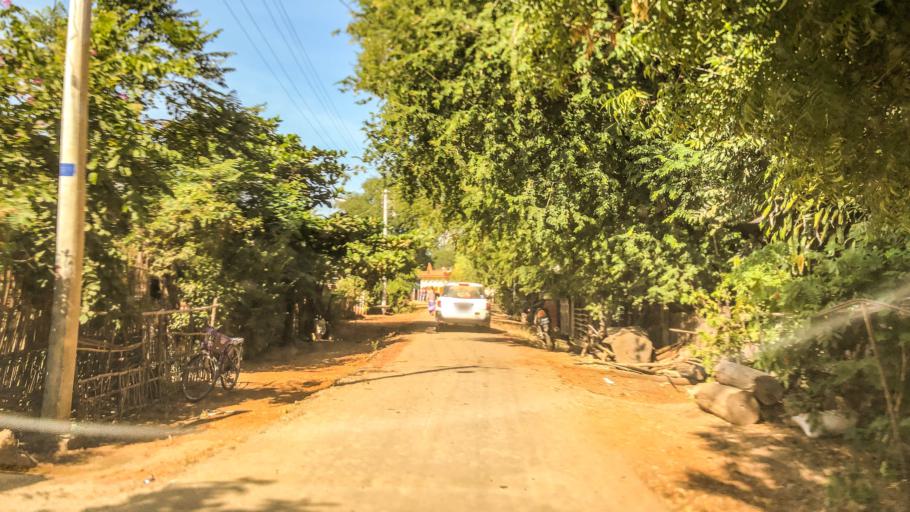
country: MM
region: Magway
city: Magway
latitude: 19.9749
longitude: 95.0377
